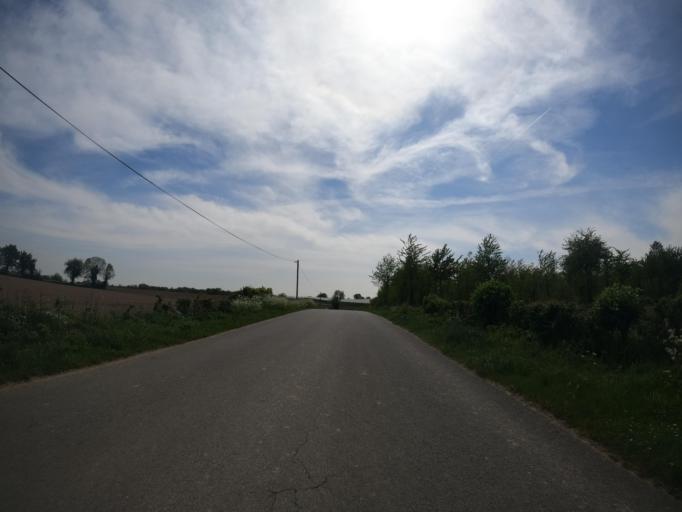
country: FR
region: Poitou-Charentes
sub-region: Departement des Deux-Sevres
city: La Chapelle-Saint-Laurent
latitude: 46.6549
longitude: -0.5068
